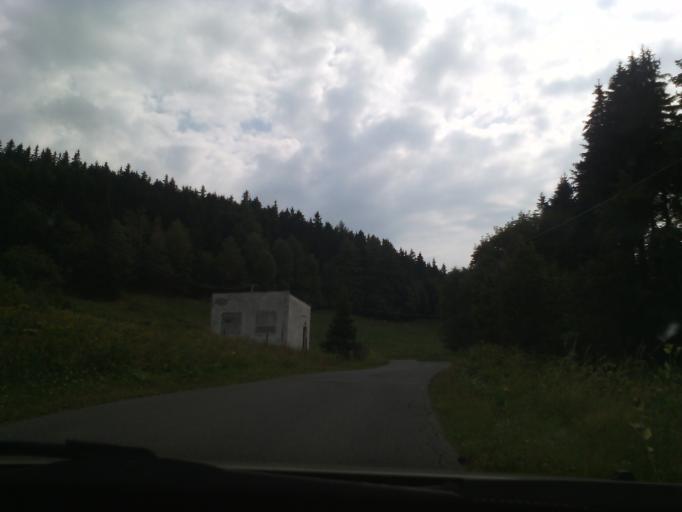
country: CZ
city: Mezimesti
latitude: 50.6898
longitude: 16.2743
